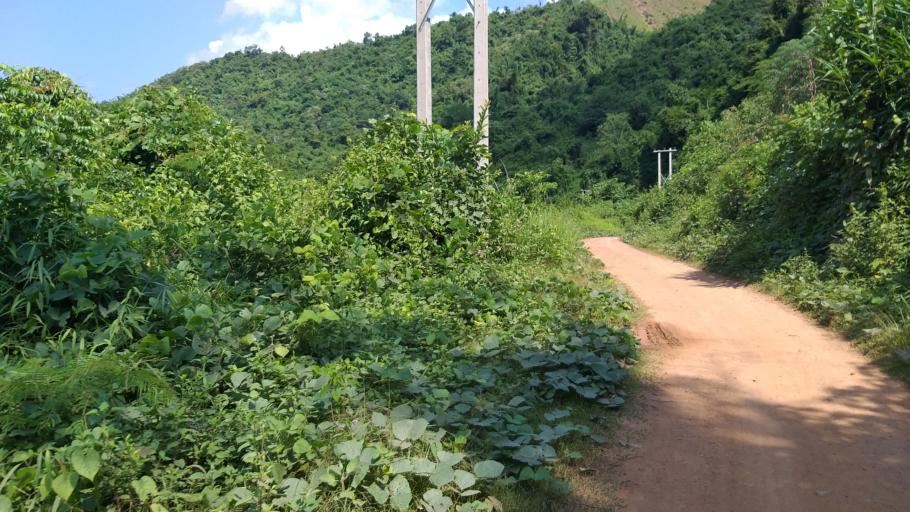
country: LA
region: Phongsali
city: Khoa
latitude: 21.3312
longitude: 102.5675
